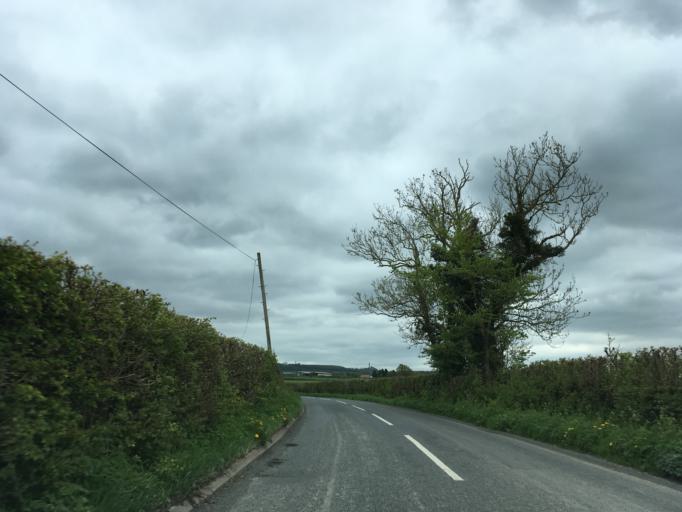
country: GB
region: England
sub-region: Gloucestershire
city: Wotton-under-Edge
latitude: 51.6184
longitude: -2.3629
